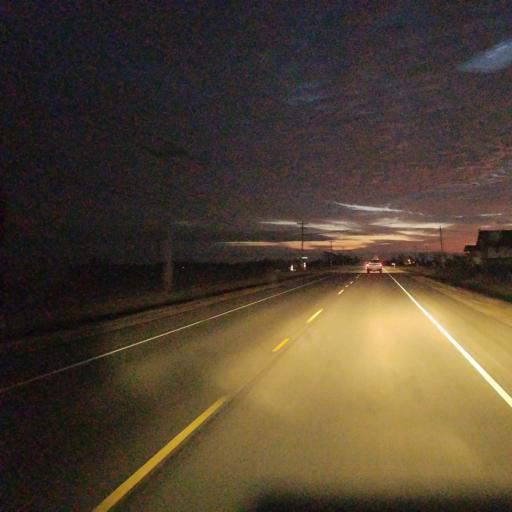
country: US
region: Illinois
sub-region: Peoria County
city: Hanna City
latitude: 40.6973
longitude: -89.8461
